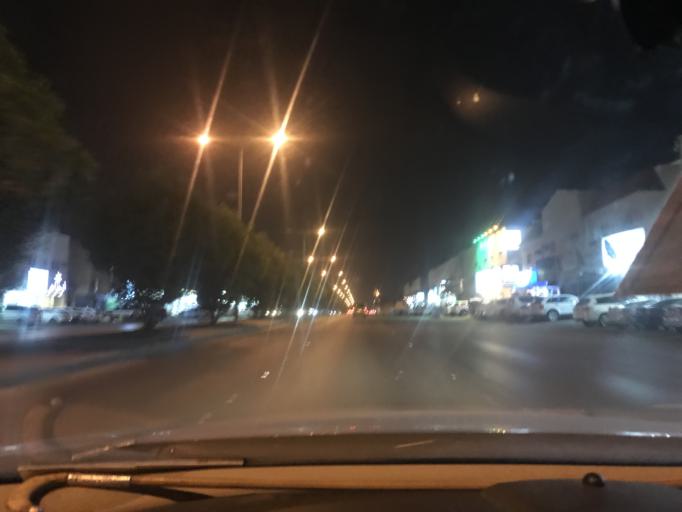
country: SA
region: Ar Riyad
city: Riyadh
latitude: 24.7554
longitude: 46.7489
